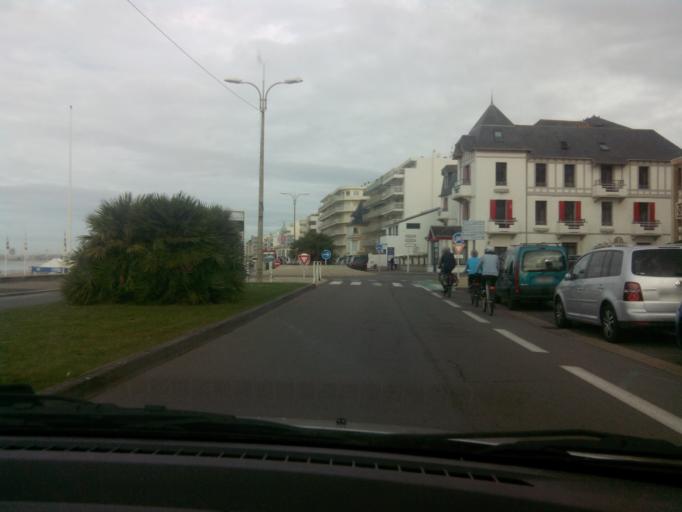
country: FR
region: Pays de la Loire
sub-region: Departement de la Loire-Atlantique
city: Pornichet
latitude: 47.2650
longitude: -2.3449
